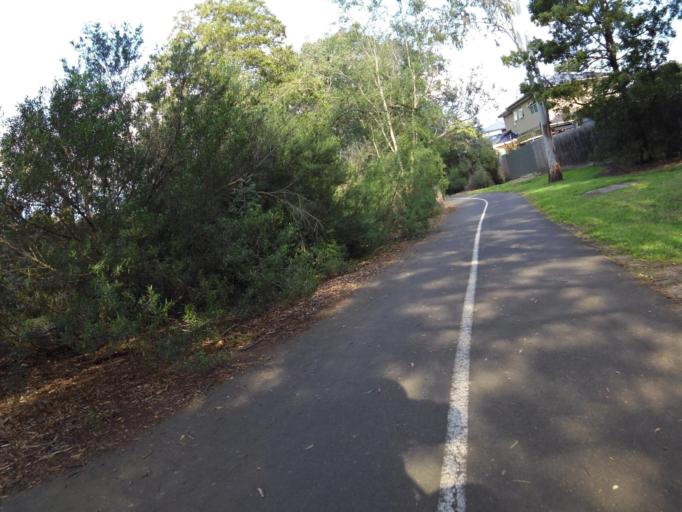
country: AU
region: Victoria
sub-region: Whitehorse
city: Box Hill North
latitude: -37.8001
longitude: 145.1194
